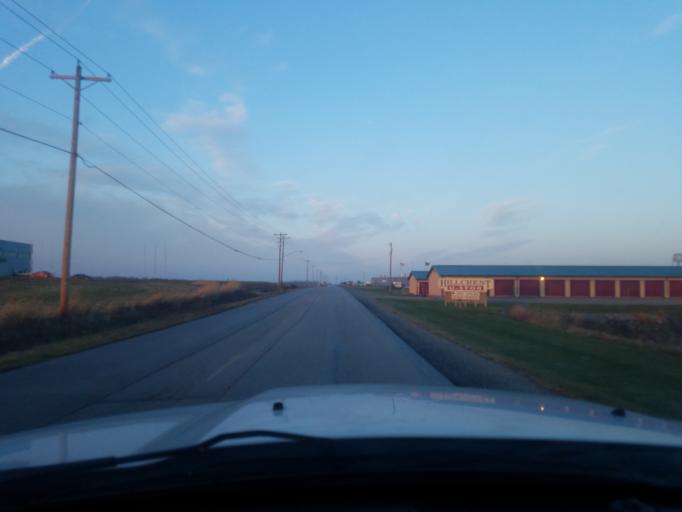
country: US
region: Indiana
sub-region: Wells County
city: Ossian
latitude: 40.8663
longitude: -85.1681
